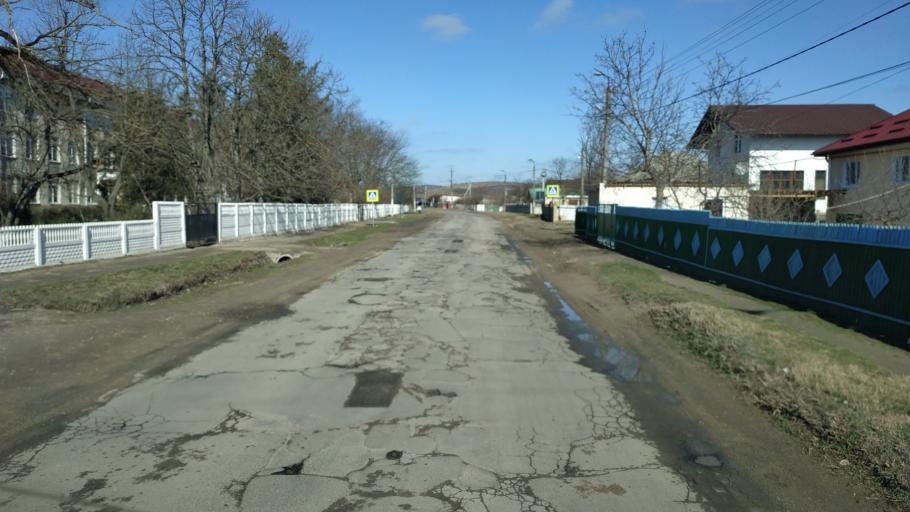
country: MD
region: Hincesti
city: Hincesti
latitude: 46.9605
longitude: 28.6032
